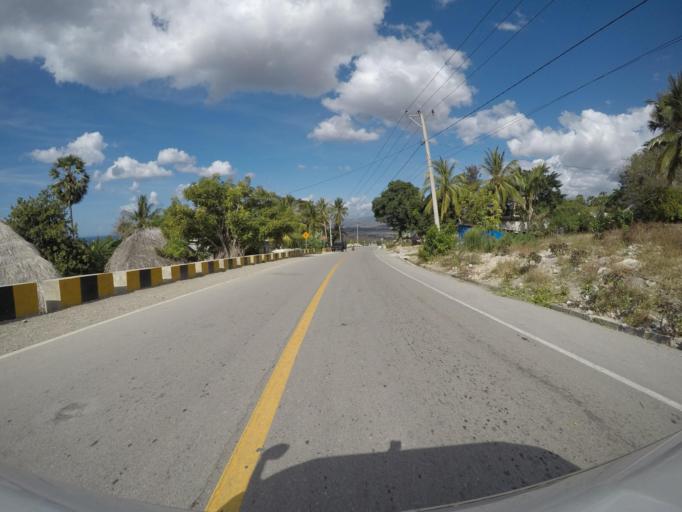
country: TL
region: Baucau
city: Baucau
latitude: -8.4697
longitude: 126.4882
